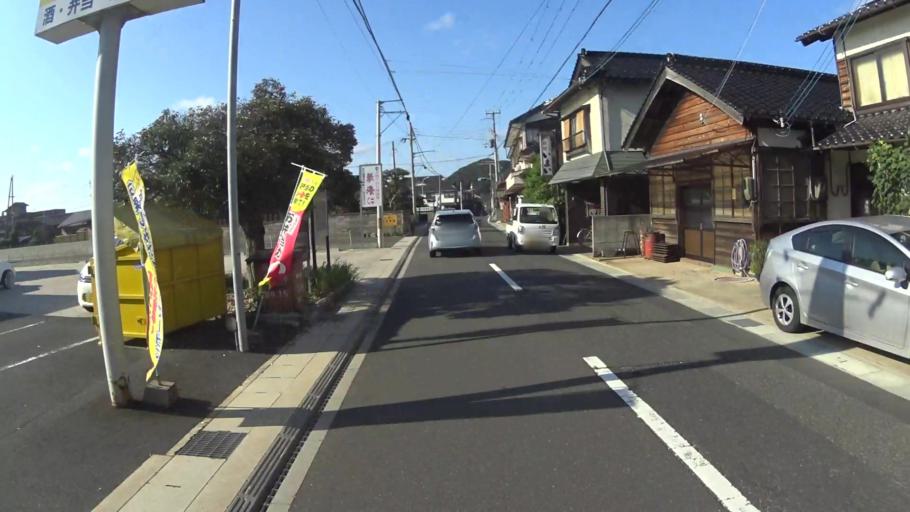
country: JP
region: Hyogo
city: Toyooka
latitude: 35.6619
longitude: 134.9687
